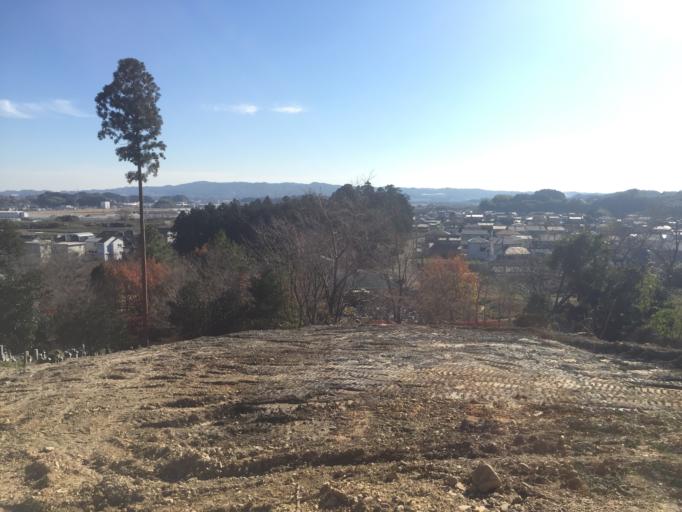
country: JP
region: Shizuoka
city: Mori
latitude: 34.7968
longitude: 137.9519
